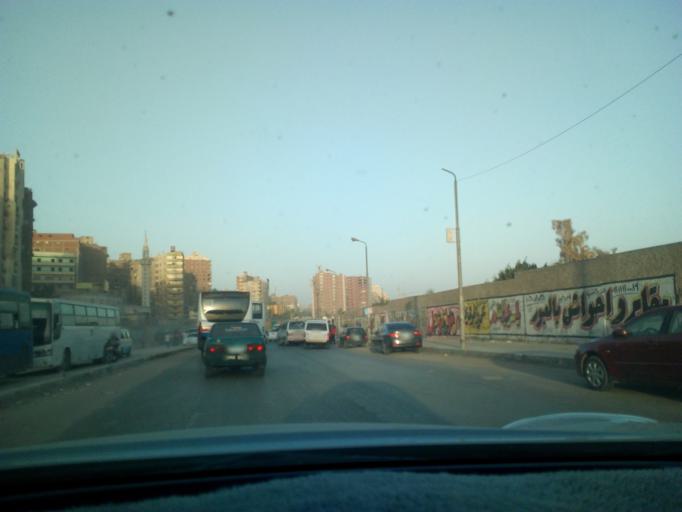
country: EG
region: Muhafazat al Qalyubiyah
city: Al Khankah
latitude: 30.1255
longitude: 31.3495
